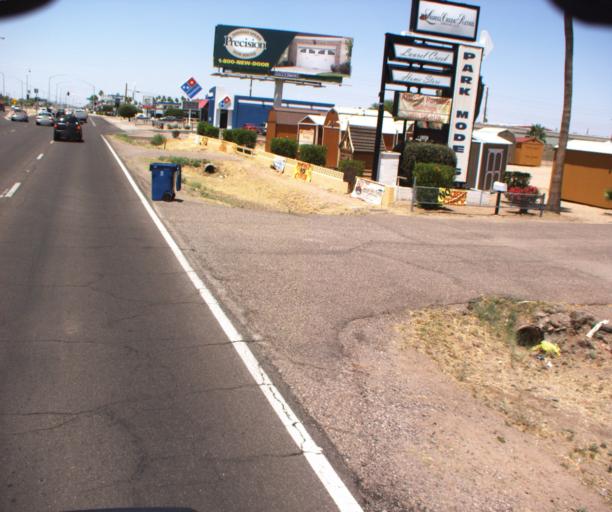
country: US
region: Arizona
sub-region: Pinal County
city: Apache Junction
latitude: 33.4154
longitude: -111.5960
